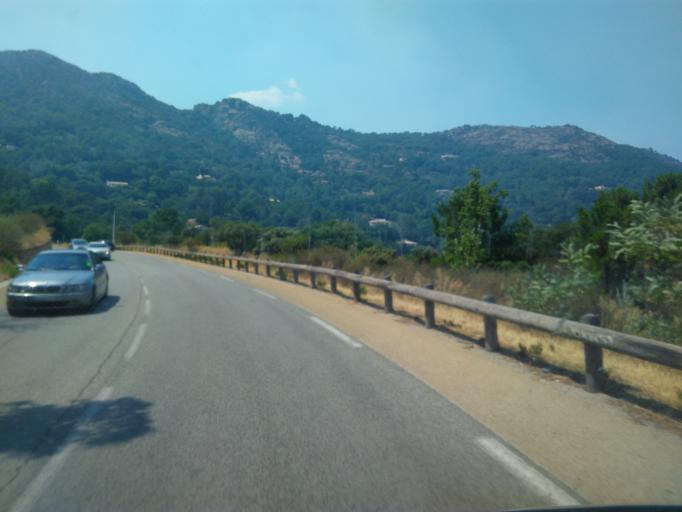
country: FR
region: Provence-Alpes-Cote d'Azur
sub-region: Departement du Var
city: La Garde-Freinet
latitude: 43.3044
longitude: 6.4734
